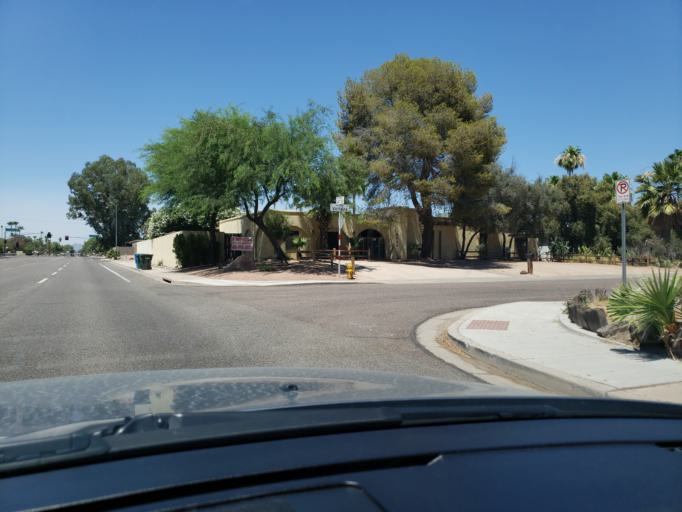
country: US
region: Arizona
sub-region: Maricopa County
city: Paradise Valley
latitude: 33.6098
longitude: -111.9432
